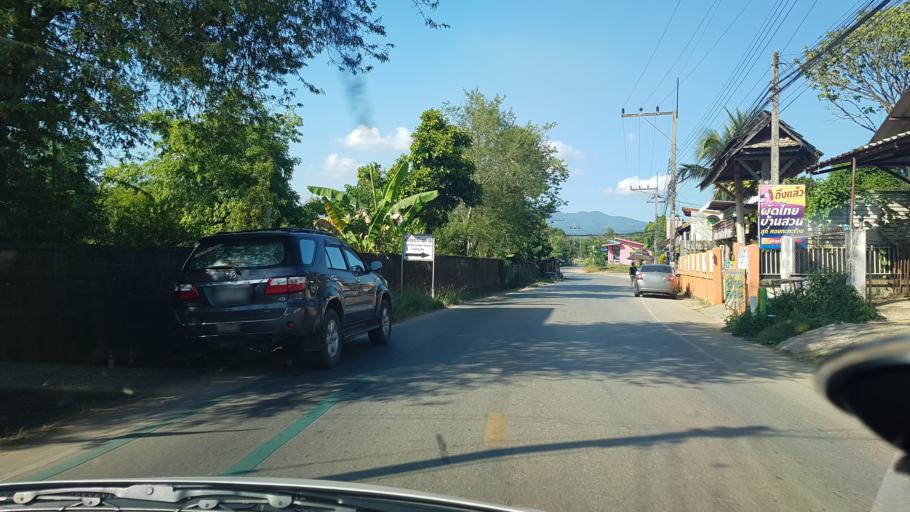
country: TH
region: Chiang Rai
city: Chiang Rai
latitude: 19.9447
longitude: 99.8107
